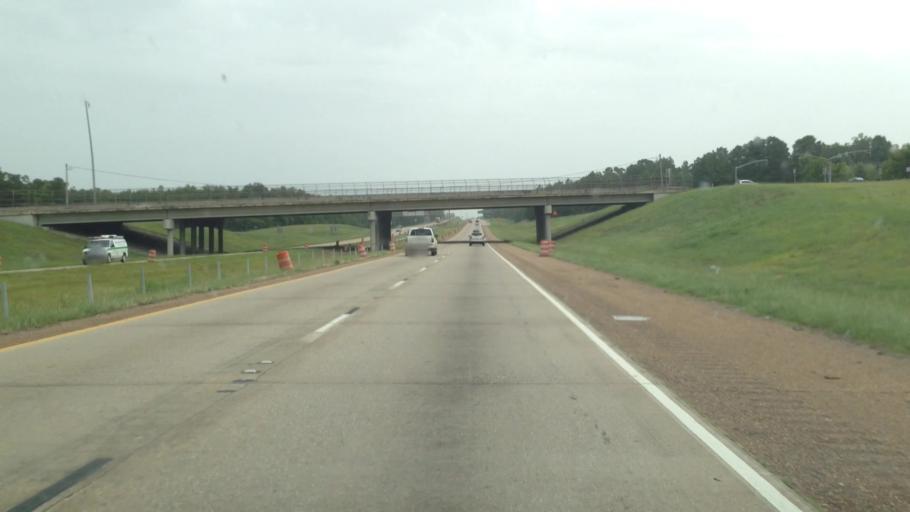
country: US
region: Louisiana
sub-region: Caddo Parish
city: Shreveport
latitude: 32.4717
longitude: -93.8382
